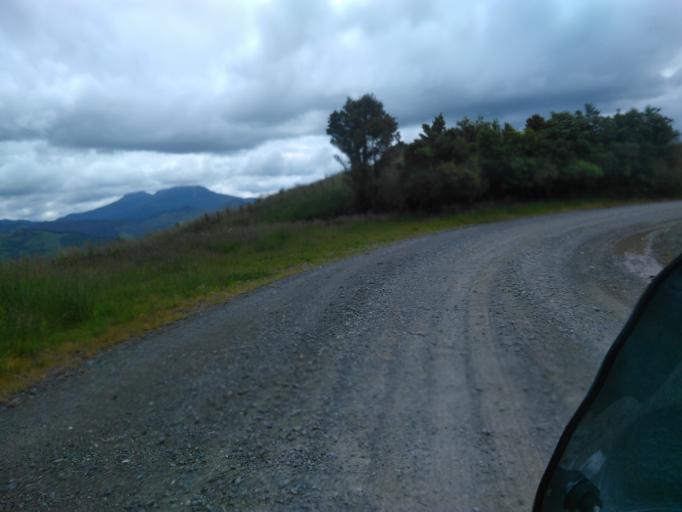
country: NZ
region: Gisborne
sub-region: Gisborne District
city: Gisborne
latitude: -38.0451
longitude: 178.0803
